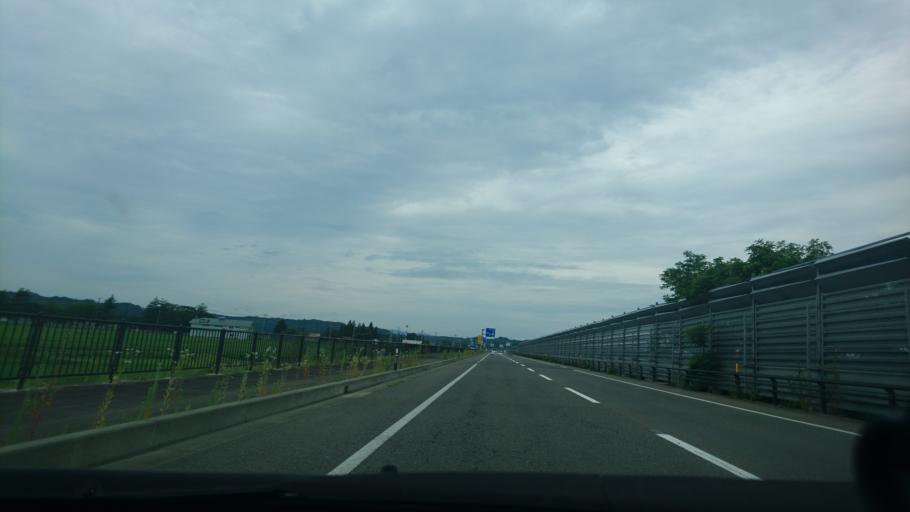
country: JP
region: Akita
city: Omagari
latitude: 39.5074
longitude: 140.3924
